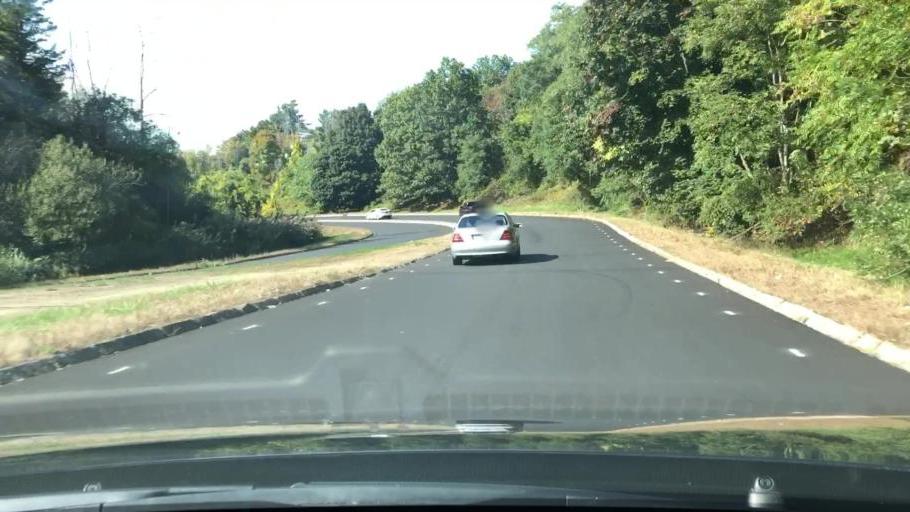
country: US
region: Massachusetts
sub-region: Essex County
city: Methuen
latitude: 42.7340
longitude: -71.1891
